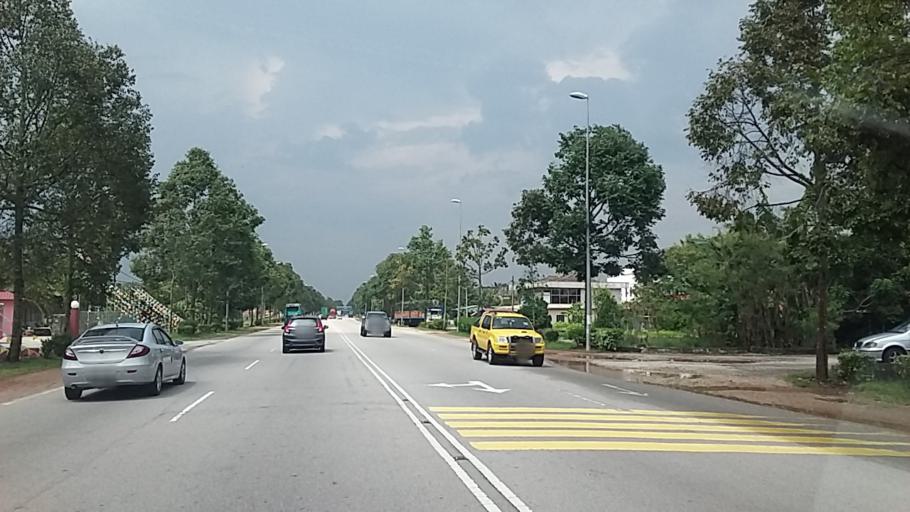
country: MY
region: Johor
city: Parit Raja
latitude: 1.8683
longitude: 103.1214
